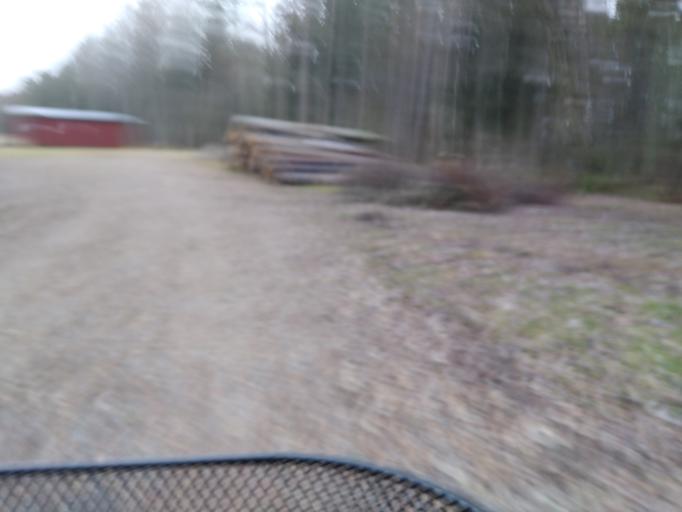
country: SE
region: Vaestra Goetaland
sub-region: Lidkopings Kommun
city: Lidkoping
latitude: 58.4855
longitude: 13.1492
